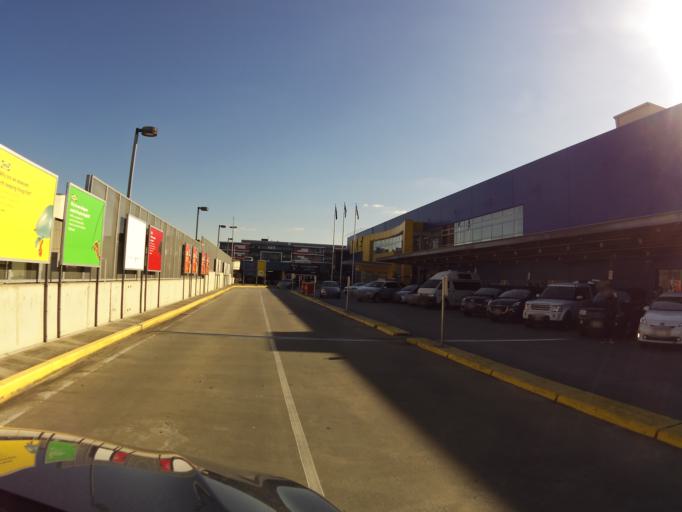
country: AU
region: Victoria
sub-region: Yarra
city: Richmond
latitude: -37.8130
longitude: 145.0115
